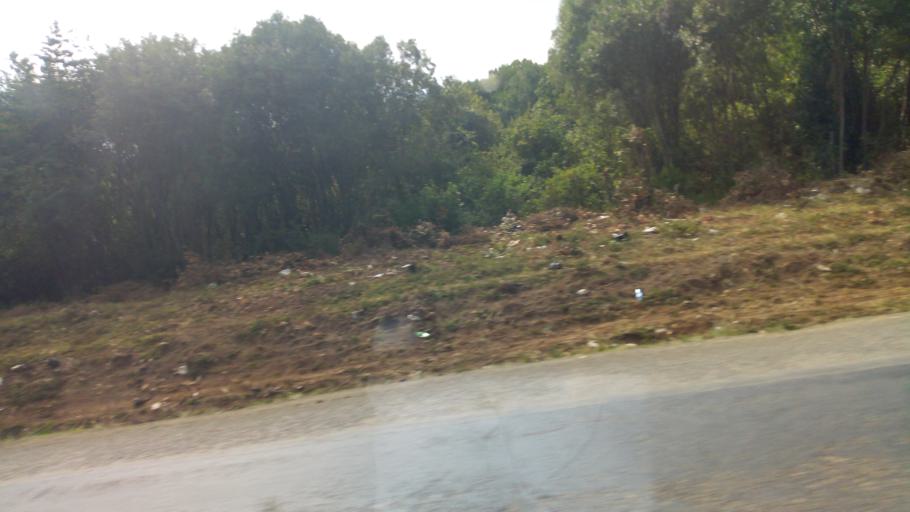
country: KE
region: Kiambu
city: Limuru
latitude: -1.0812
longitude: 36.6032
